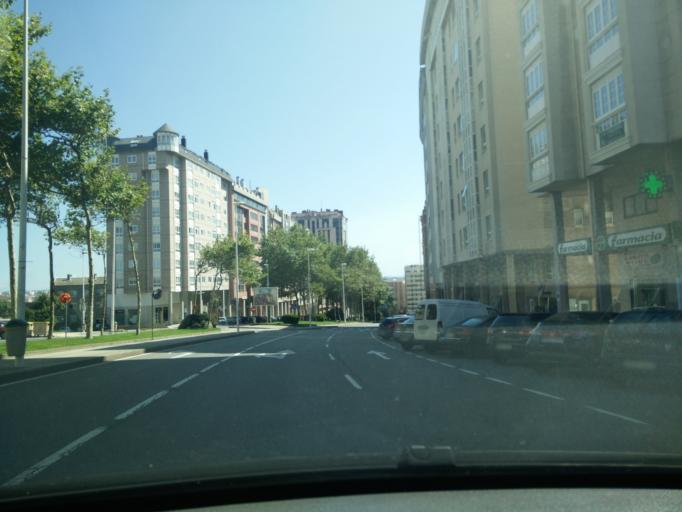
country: ES
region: Galicia
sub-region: Provincia da Coruna
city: A Coruna
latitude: 43.3750
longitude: -8.4283
